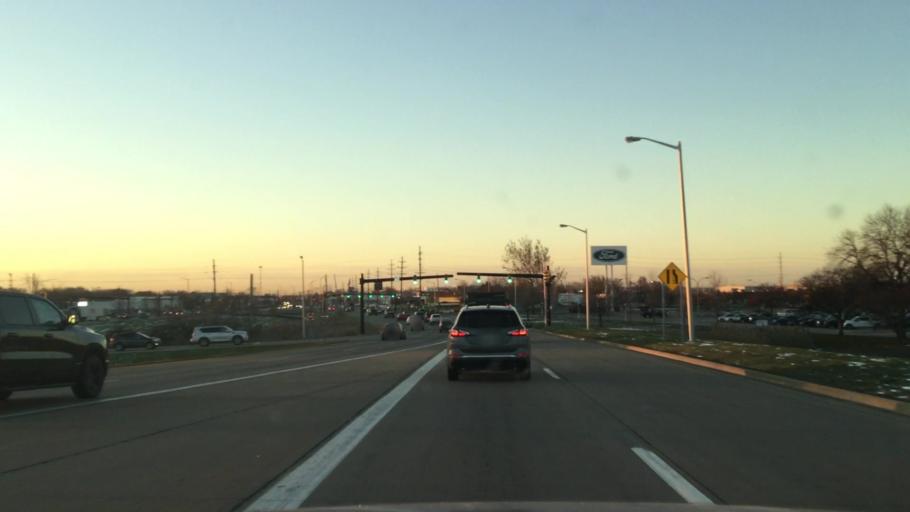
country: US
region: Michigan
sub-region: Macomb County
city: Sterling Heights
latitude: 42.5976
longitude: -83.0307
